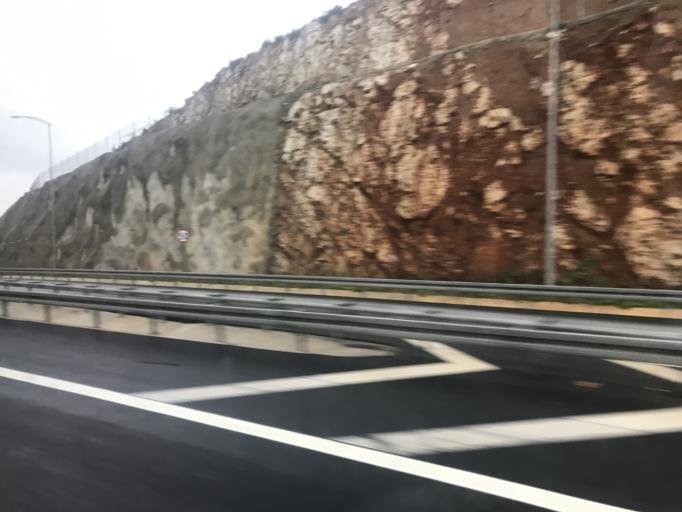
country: TR
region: Bursa
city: Umurbey
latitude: 40.4301
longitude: 29.2309
